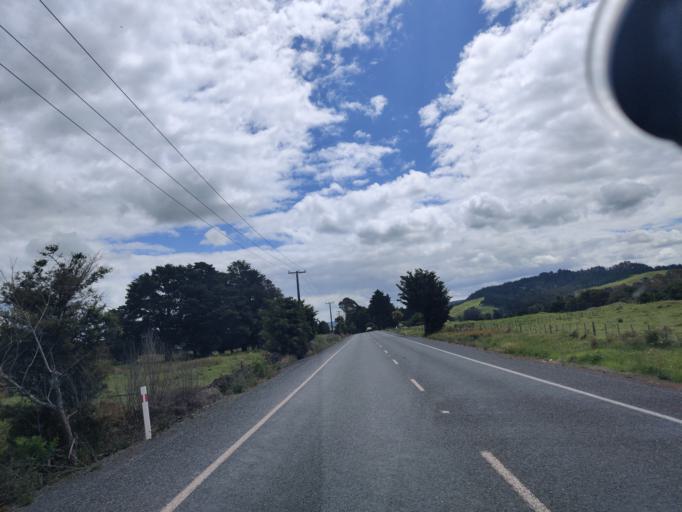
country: NZ
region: Northland
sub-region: Far North District
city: Kerikeri
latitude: -35.2944
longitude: 173.9797
